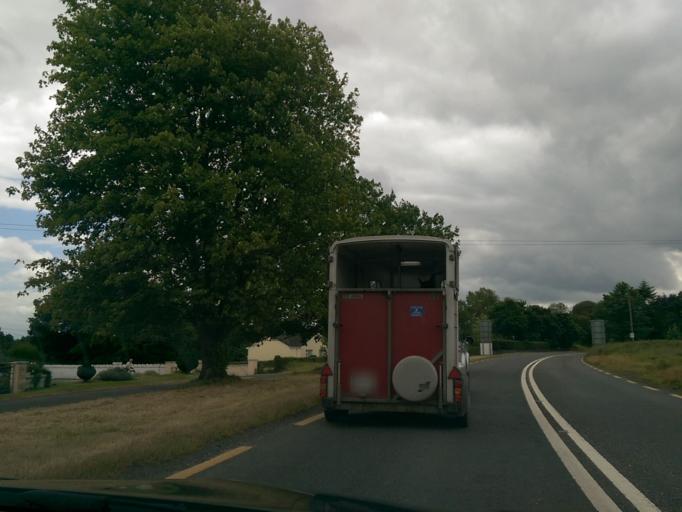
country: IE
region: Munster
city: Thurles
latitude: 52.6565
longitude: -7.7998
